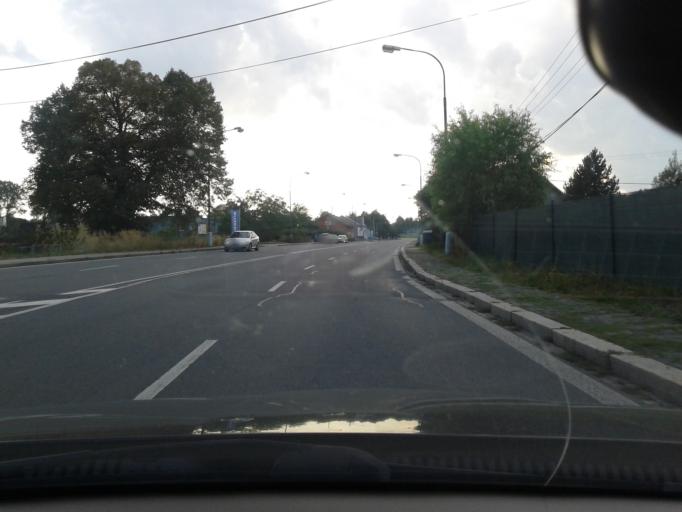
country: CZ
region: Moravskoslezsky
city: Orlova
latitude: 49.8400
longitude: 18.4117
